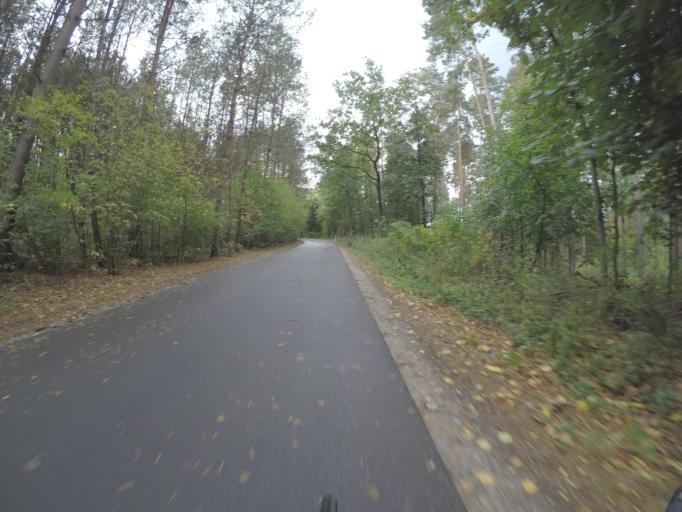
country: DE
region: Brandenburg
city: Strausberg
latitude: 52.5976
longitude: 13.9075
